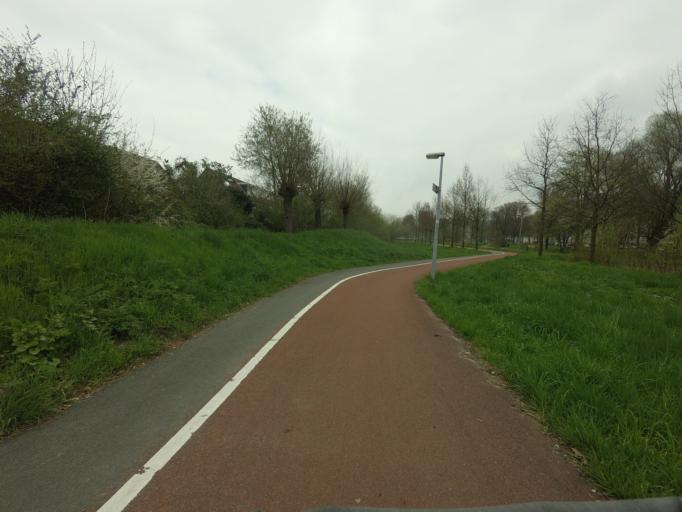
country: NL
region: Utrecht
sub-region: Gemeente Utrecht
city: Utrecht
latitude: 52.1213
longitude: 5.0932
